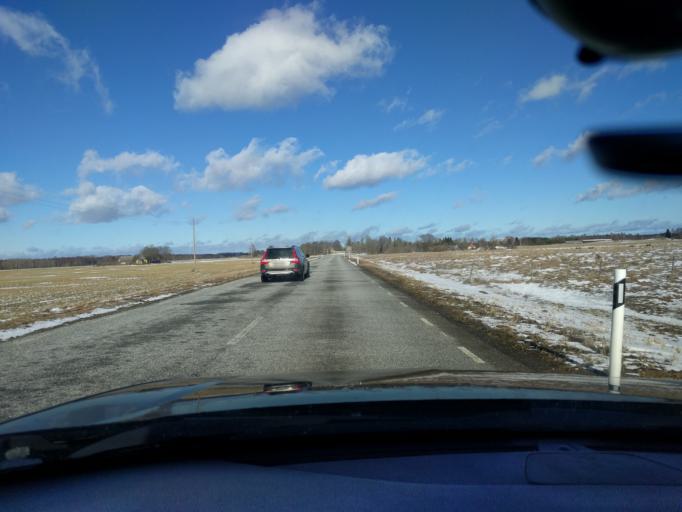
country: EE
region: Harju
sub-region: Raasiku vald
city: Raasiku
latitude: 59.3912
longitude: 25.1878
